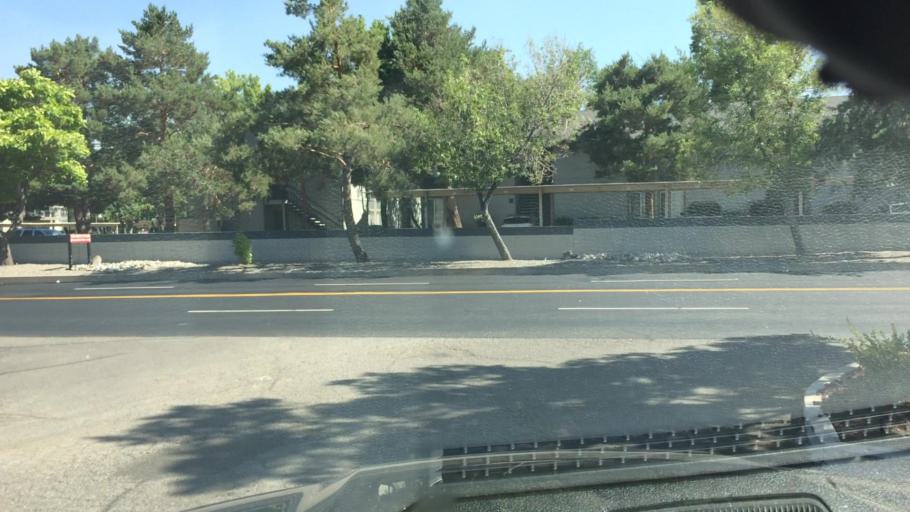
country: US
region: Nevada
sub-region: Washoe County
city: Reno
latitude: 39.4717
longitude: -119.7834
